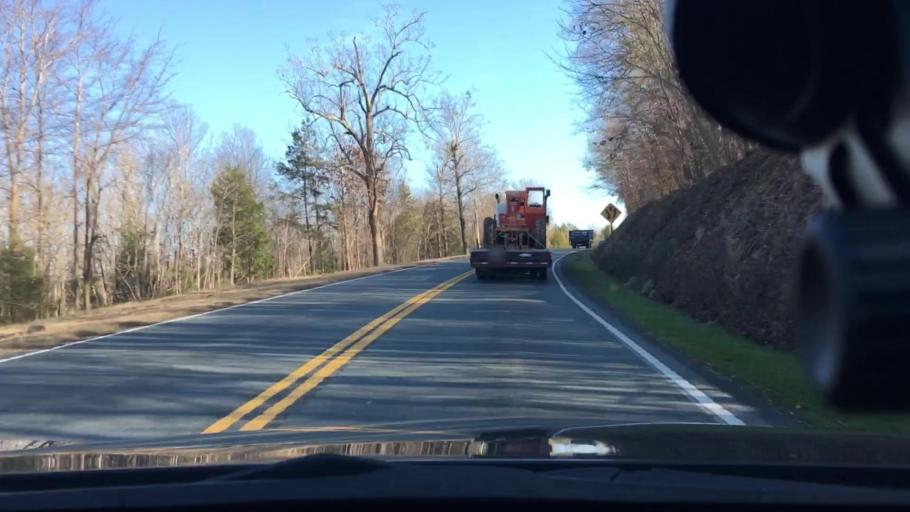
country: US
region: North Carolina
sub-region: Stanly County
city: Norwood
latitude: 35.3112
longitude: -80.0876
